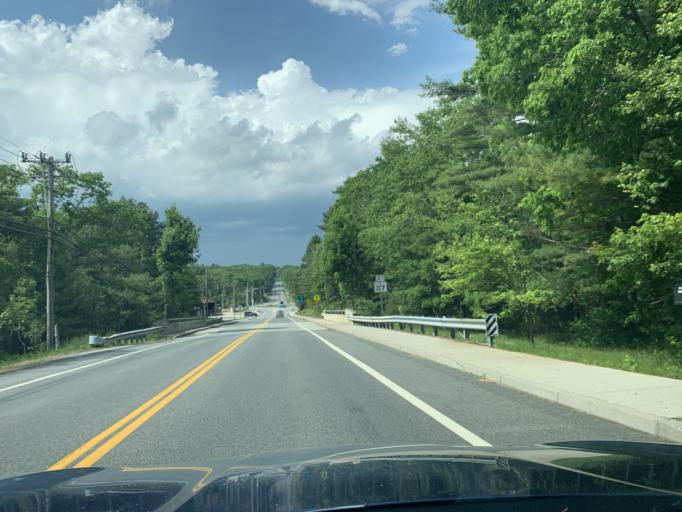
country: US
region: Rhode Island
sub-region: Kent County
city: Coventry
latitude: 41.6904
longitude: -71.6933
